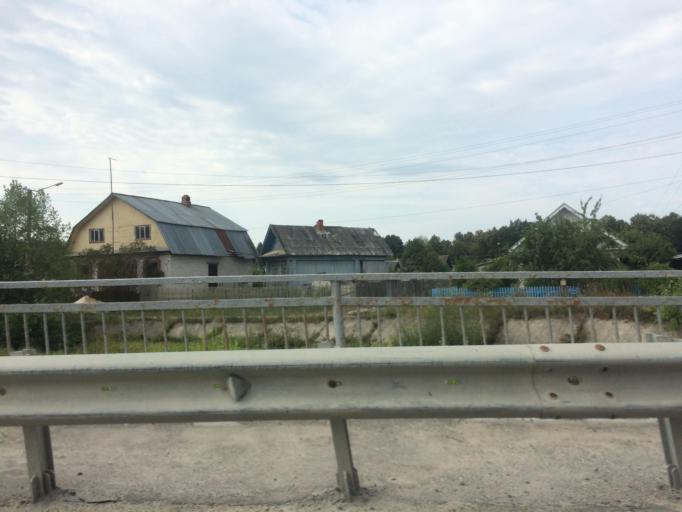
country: RU
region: Mariy-El
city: Yoshkar-Ola
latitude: 56.5556
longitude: 47.9845
